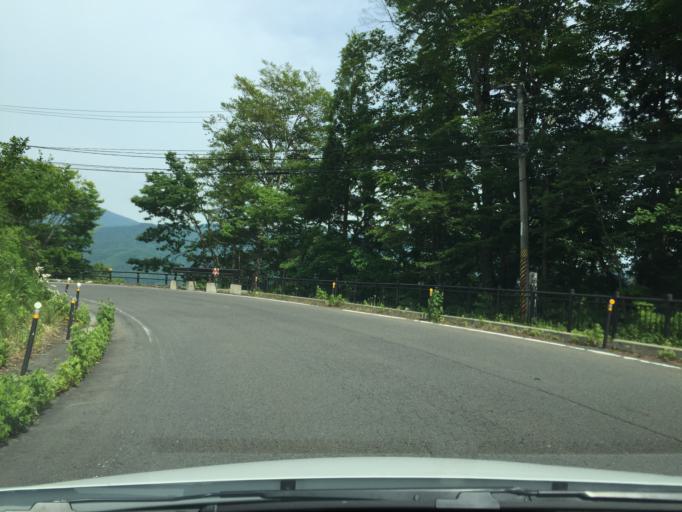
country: JP
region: Fukushima
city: Inawashiro
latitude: 37.7226
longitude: 140.0411
